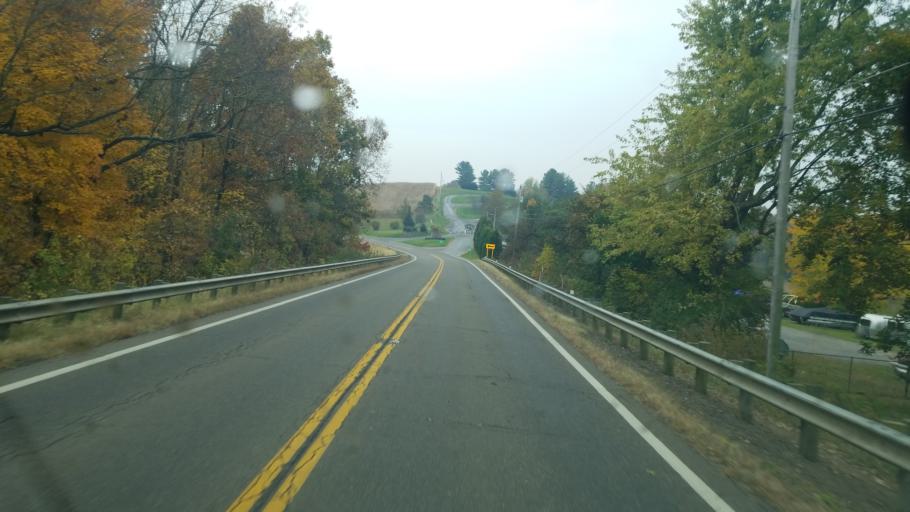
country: US
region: Ohio
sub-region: Holmes County
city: Millersburg
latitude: 40.4650
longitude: -81.9030
